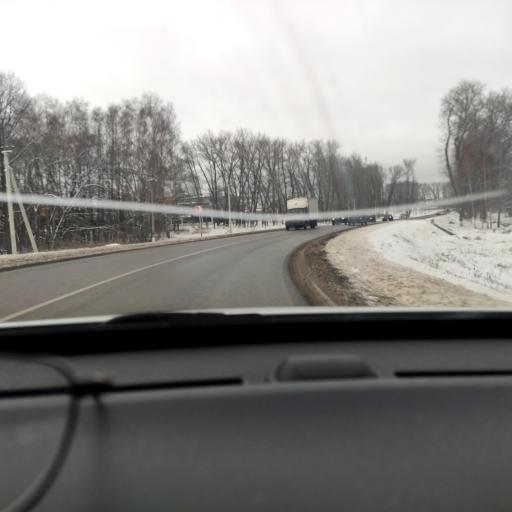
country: RU
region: Voronezj
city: Novaya Usman'
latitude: 51.6789
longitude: 39.4035
